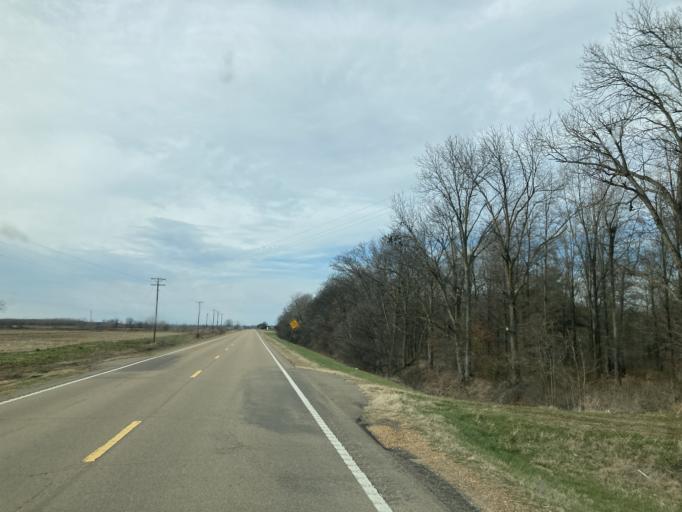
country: US
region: Mississippi
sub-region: Humphreys County
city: Belzoni
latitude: 33.1827
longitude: -90.6295
